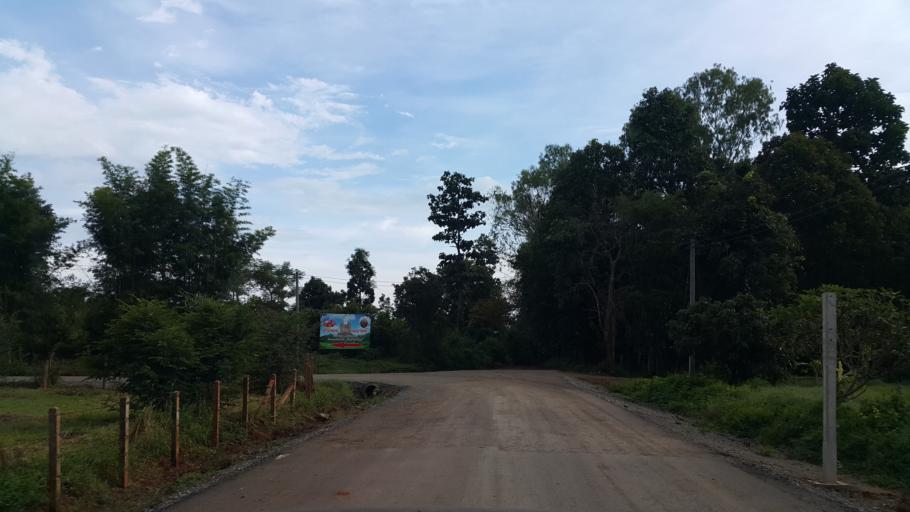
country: TH
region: Chiang Mai
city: Mae On
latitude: 18.8937
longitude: 99.2298
